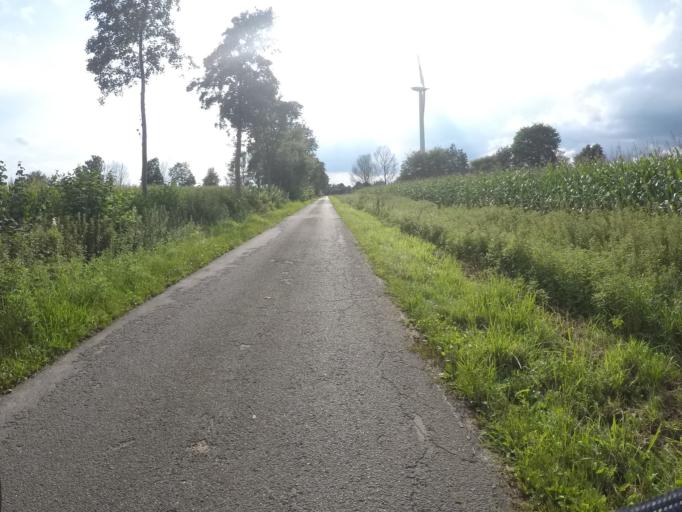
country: DE
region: North Rhine-Westphalia
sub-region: Regierungsbezirk Dusseldorf
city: Bocholt
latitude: 51.8209
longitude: 6.5432
